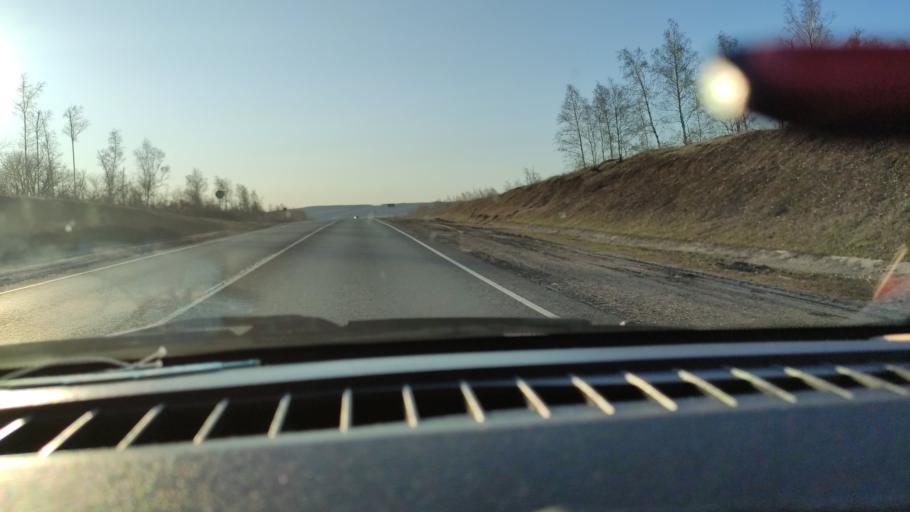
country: RU
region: Saratov
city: Shikhany
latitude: 52.1218
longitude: 47.2590
